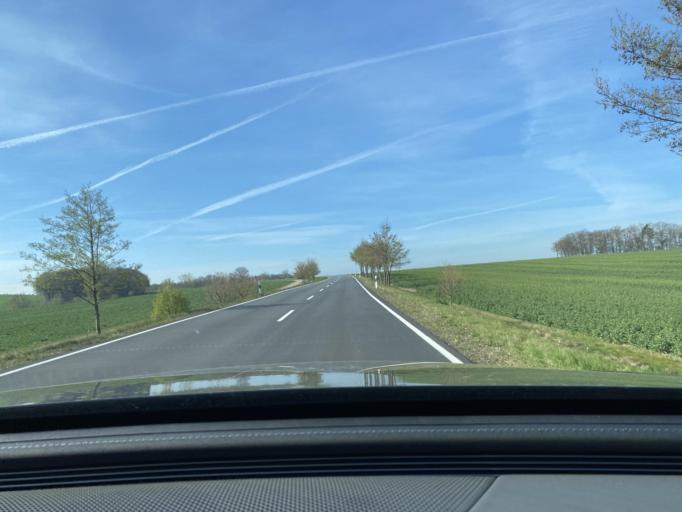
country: DE
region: Saxony
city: Radibor
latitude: 51.2206
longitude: 14.3763
